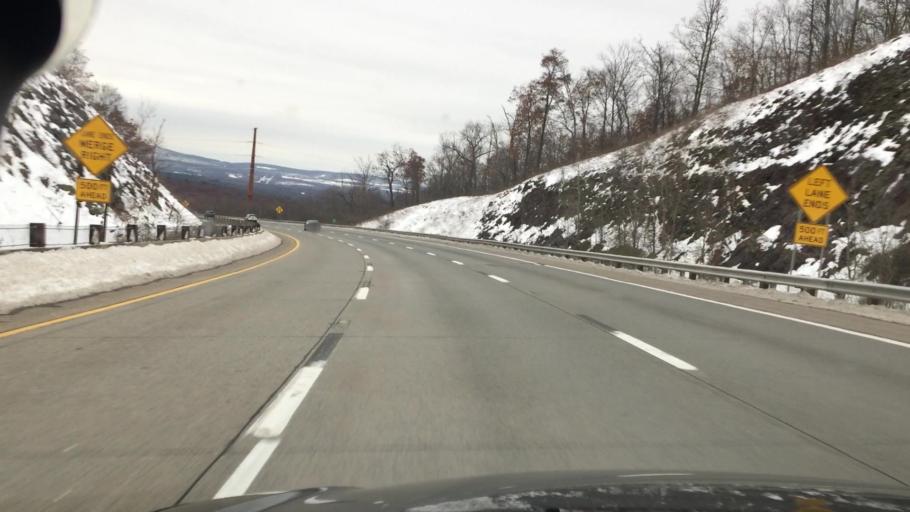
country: US
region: Pennsylvania
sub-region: Luzerne County
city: Nanticoke
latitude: 41.1710
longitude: -75.9573
